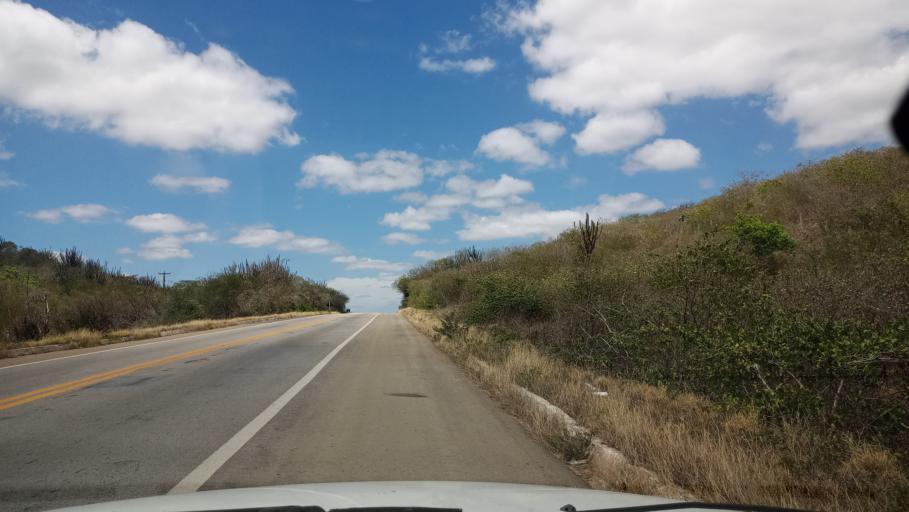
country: BR
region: Rio Grande do Norte
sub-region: Sao Paulo Do Potengi
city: Sao Paulo do Potengi
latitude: -5.7484
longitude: -35.9087
